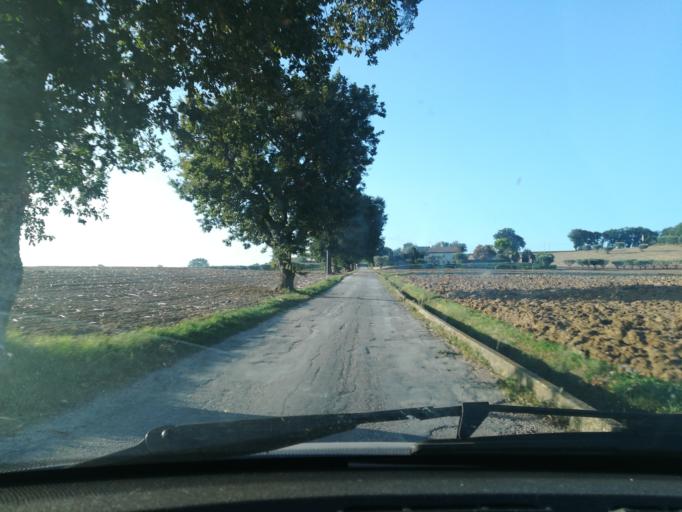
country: IT
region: The Marches
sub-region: Provincia di Macerata
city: Piediripa
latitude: 43.2758
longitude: 13.4653
